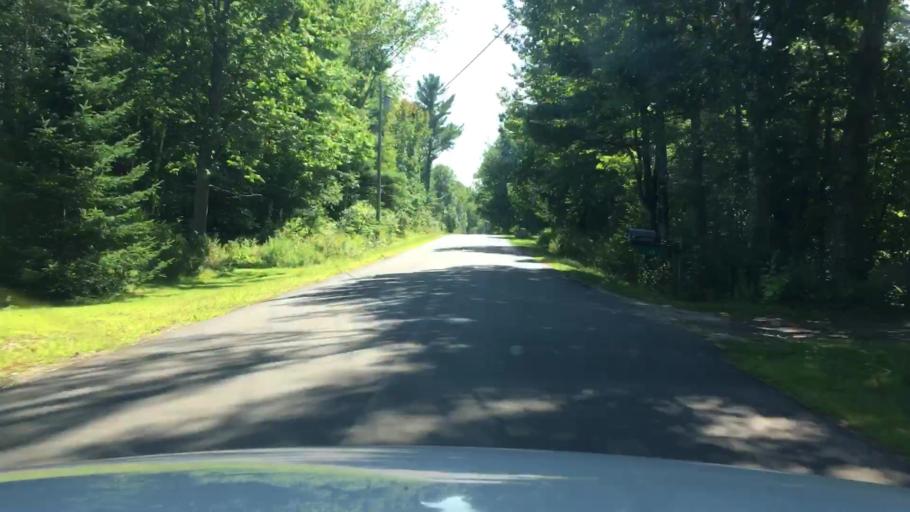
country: US
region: Maine
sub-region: Kennebec County
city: Monmouth
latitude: 44.2620
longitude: -70.0544
